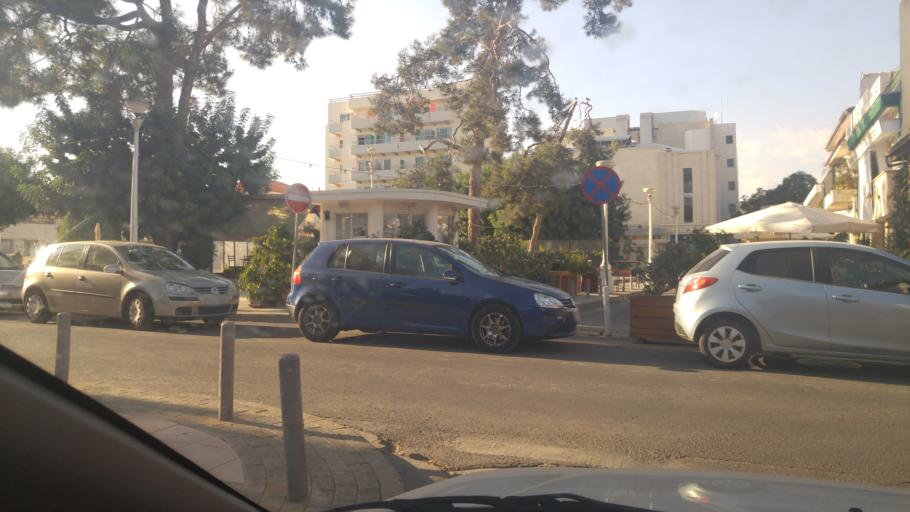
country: CY
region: Limassol
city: Limassol
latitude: 34.6791
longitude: 33.0463
